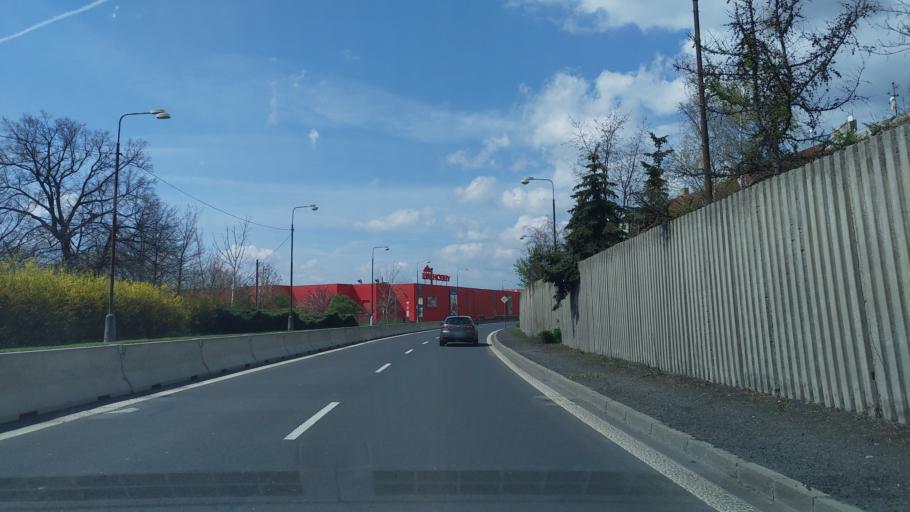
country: CZ
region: Ustecky
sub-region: Okres Chomutov
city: Chomutov
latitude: 50.4583
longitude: 13.3999
